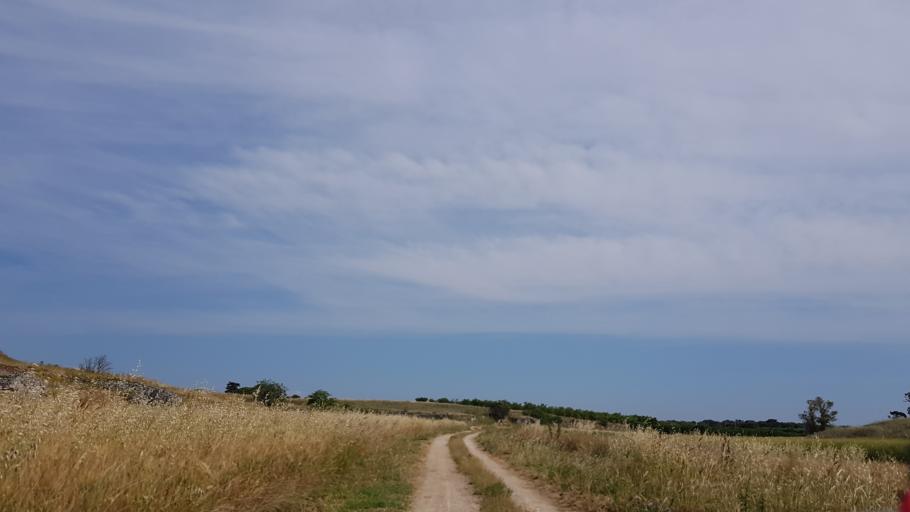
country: IT
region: Apulia
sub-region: Provincia di Brindisi
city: San Vito dei Normanni
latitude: 40.6635
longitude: 17.7980
